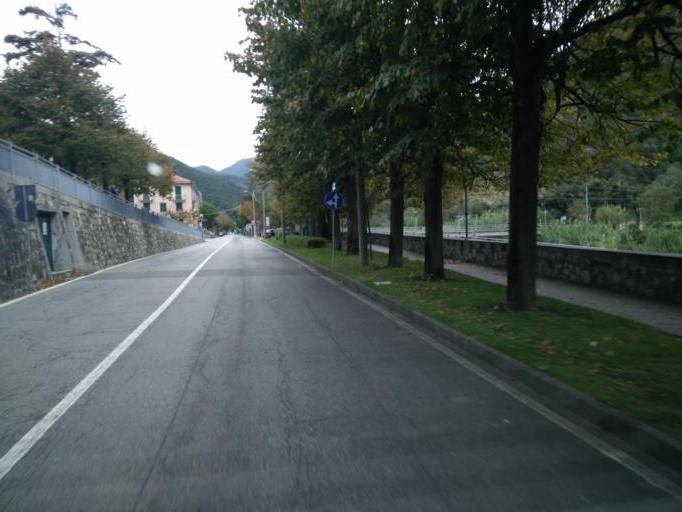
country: IT
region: Liguria
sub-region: Provincia di La Spezia
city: Deiva Marina
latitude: 44.2173
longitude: 9.5195
